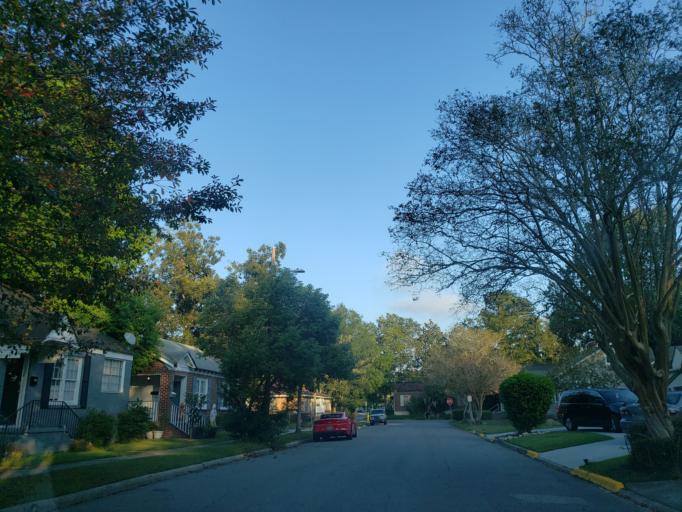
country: US
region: Georgia
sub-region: Chatham County
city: Savannah
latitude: 32.0551
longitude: -81.0852
